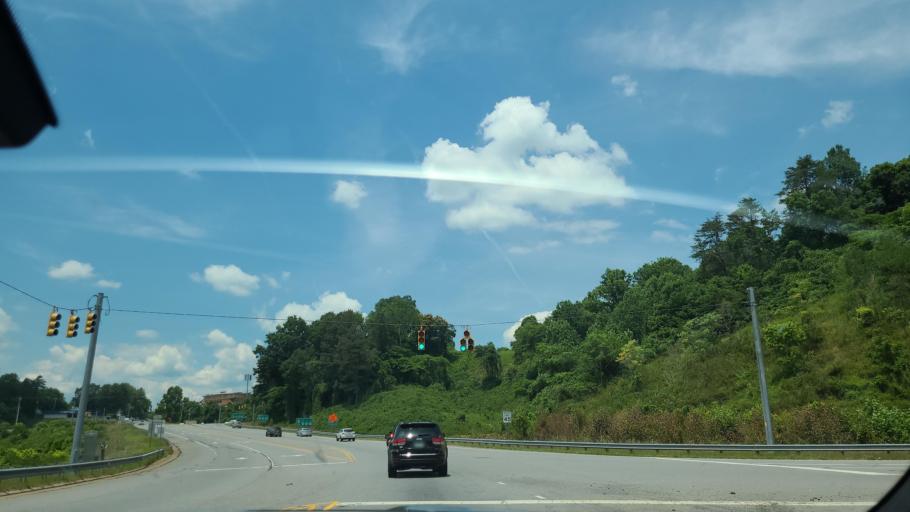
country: US
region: North Carolina
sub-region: Cherokee County
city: Murphy
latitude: 35.0795
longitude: -84.0261
